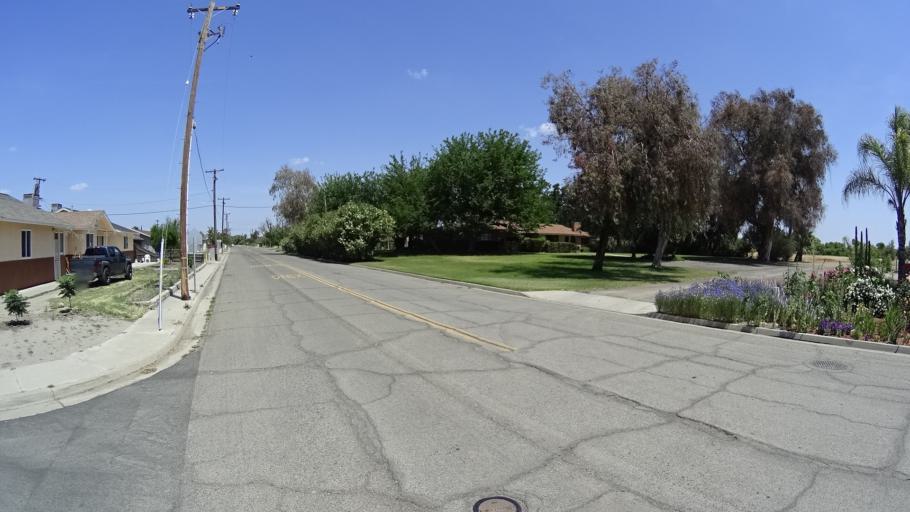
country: US
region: California
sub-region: Kings County
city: Stratford
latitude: 36.1931
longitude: -119.8206
